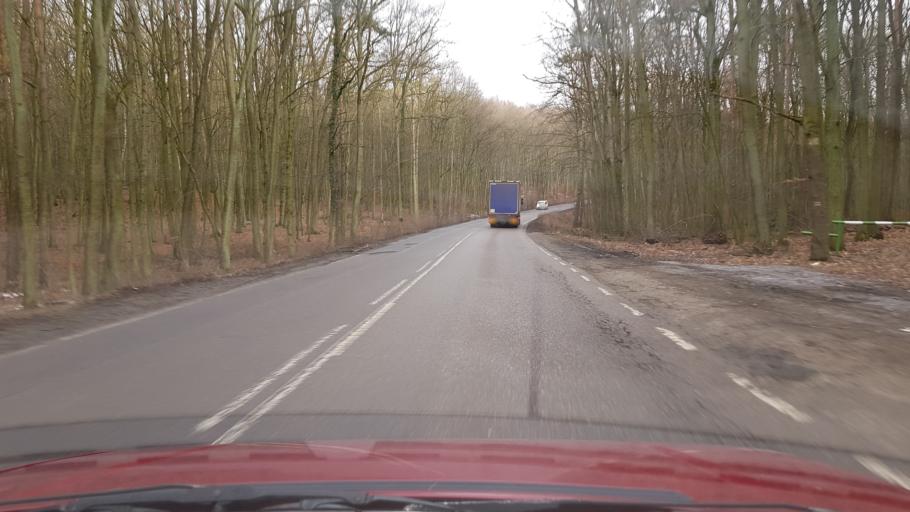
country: PL
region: West Pomeranian Voivodeship
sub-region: Powiat policki
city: Police
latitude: 53.5231
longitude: 14.5686
